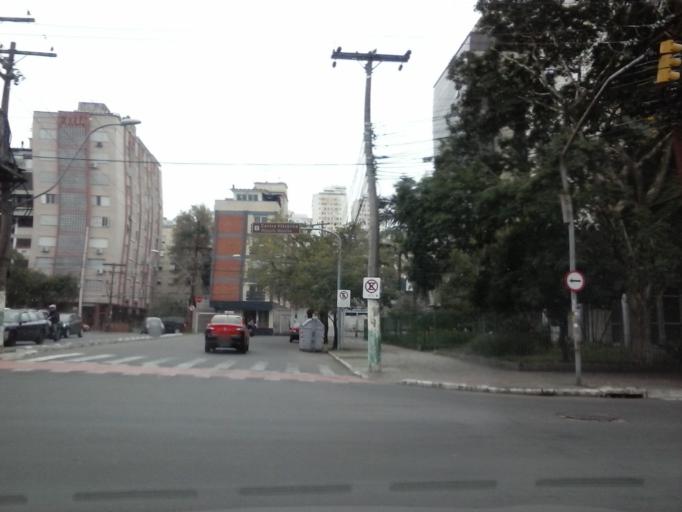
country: BR
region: Rio Grande do Sul
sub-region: Porto Alegre
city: Porto Alegre
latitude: -30.0373
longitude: -51.2327
